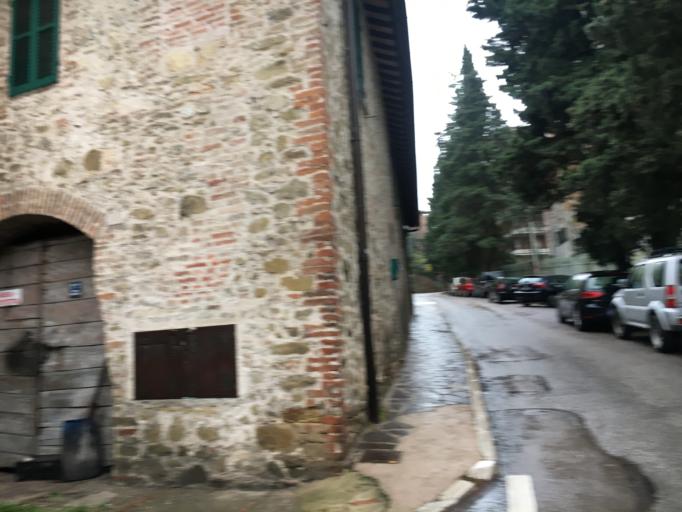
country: IT
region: Umbria
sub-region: Provincia di Perugia
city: Perugia
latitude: 43.1137
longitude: 12.3784
